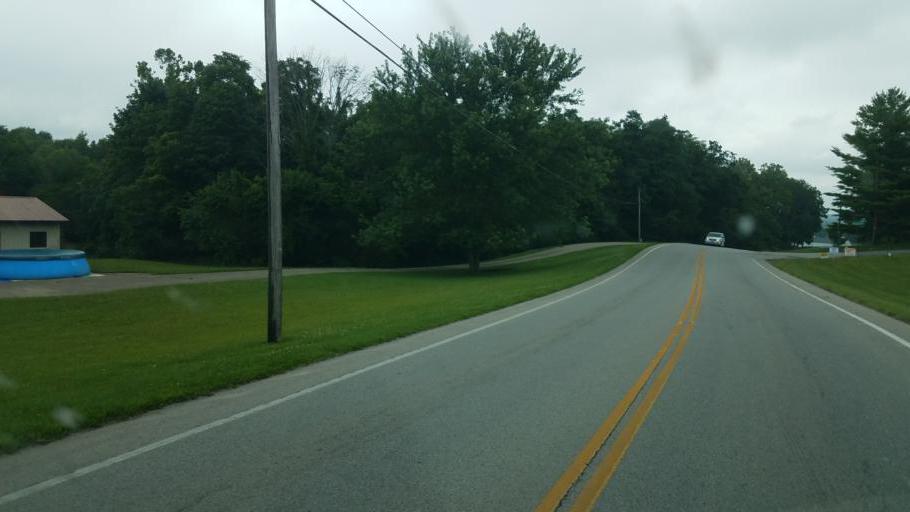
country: US
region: Ohio
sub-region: Highland County
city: Hillsboro
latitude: 39.2085
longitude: -83.5692
